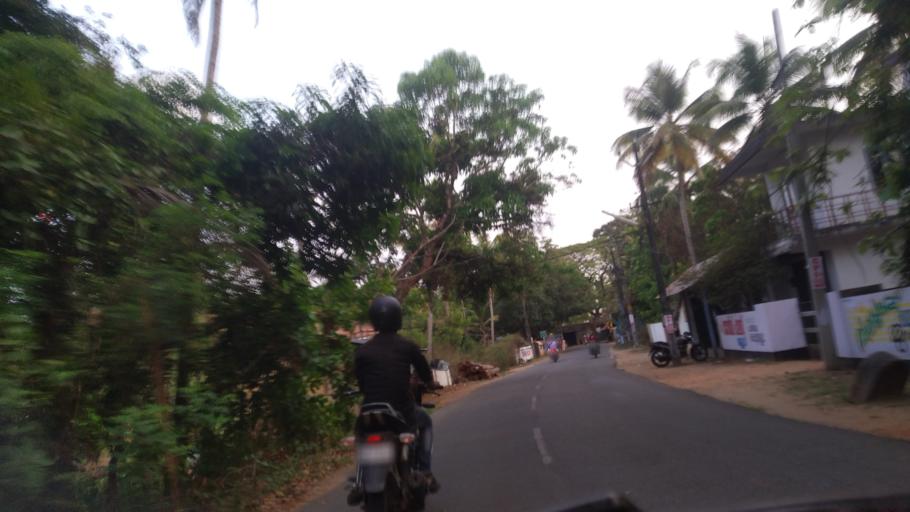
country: IN
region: Kerala
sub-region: Thrissur District
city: Kodungallur
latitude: 10.2293
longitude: 76.1548
